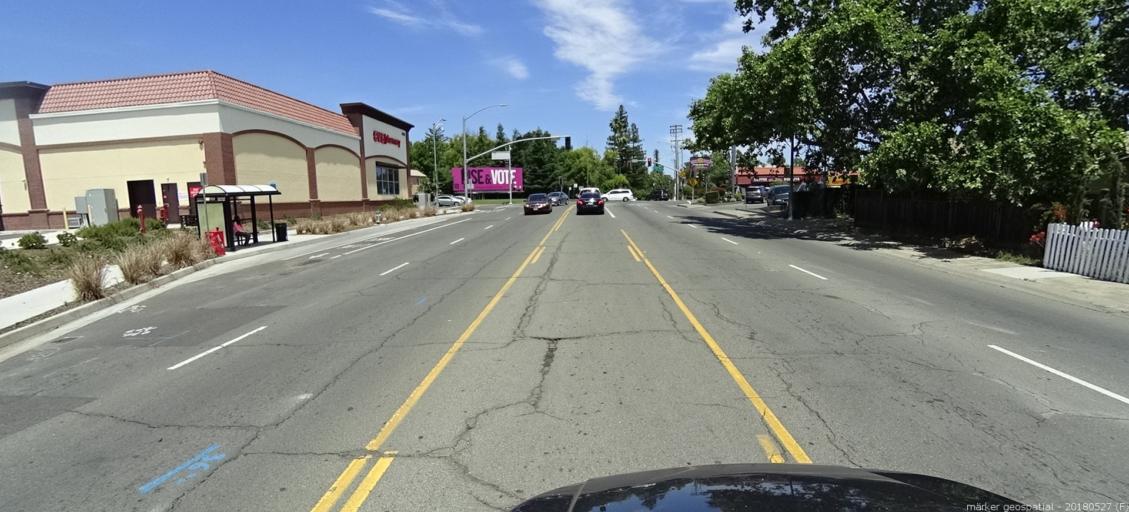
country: US
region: California
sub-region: Sacramento County
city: Sacramento
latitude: 38.5404
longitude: -121.4756
